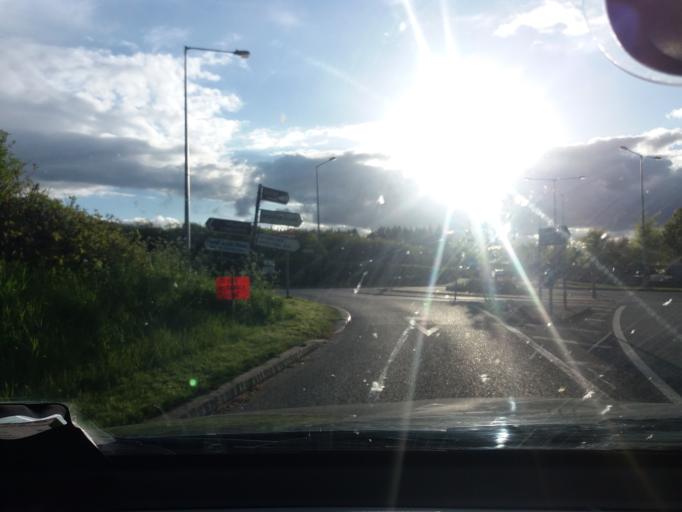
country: IE
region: Leinster
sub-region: South Dublin
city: Rathcoole
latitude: 53.2937
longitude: -6.4800
